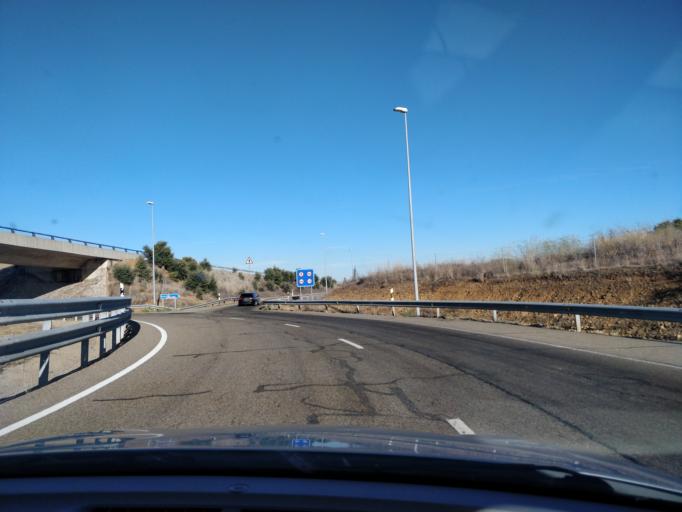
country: ES
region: Castille and Leon
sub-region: Provincia de Leon
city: San Andres del Rabanedo
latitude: 42.5760
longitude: -5.6205
